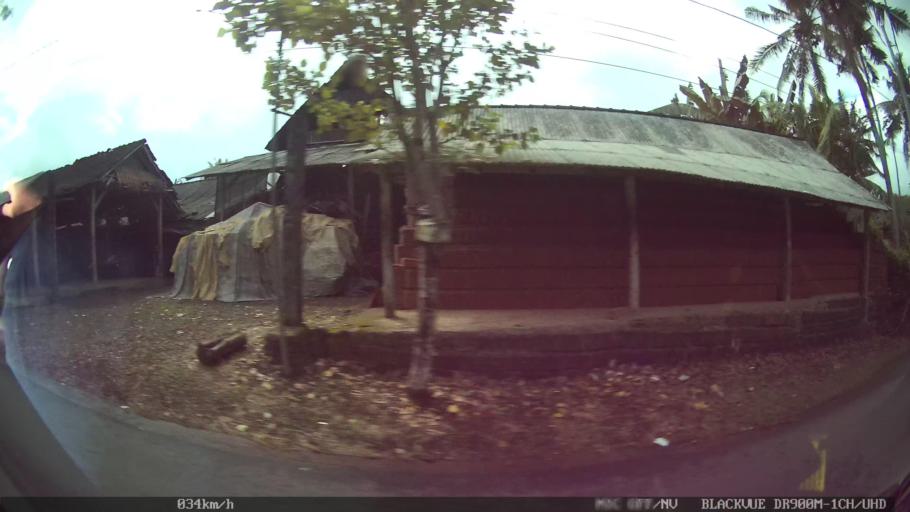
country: ID
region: Bali
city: Banjar Parekan
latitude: -8.5696
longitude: 115.2027
